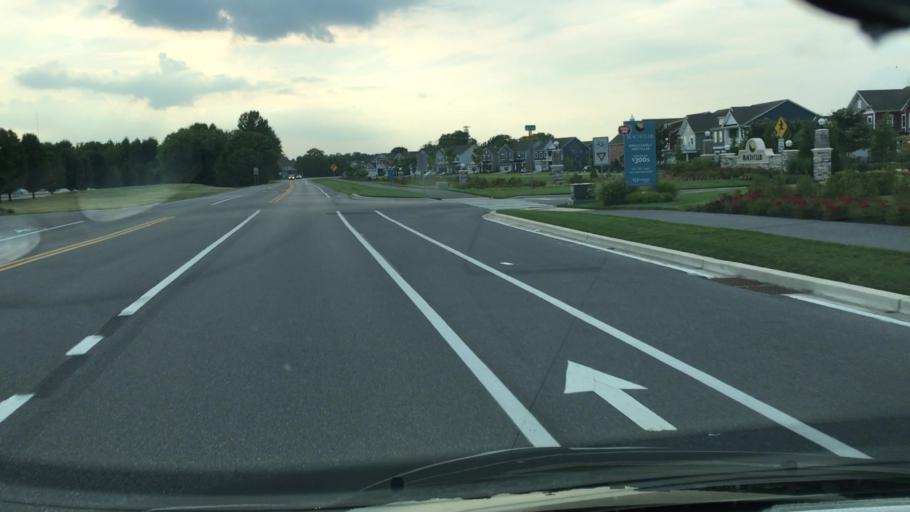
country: US
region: Delaware
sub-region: Sussex County
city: Ocean View
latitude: 38.5256
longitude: -75.0765
